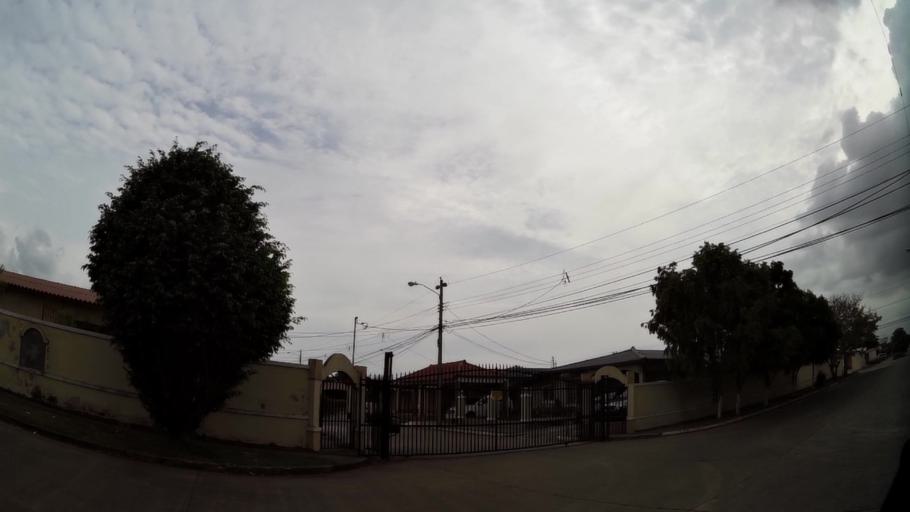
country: PA
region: Panama
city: Tocumen
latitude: 9.0431
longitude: -79.4052
